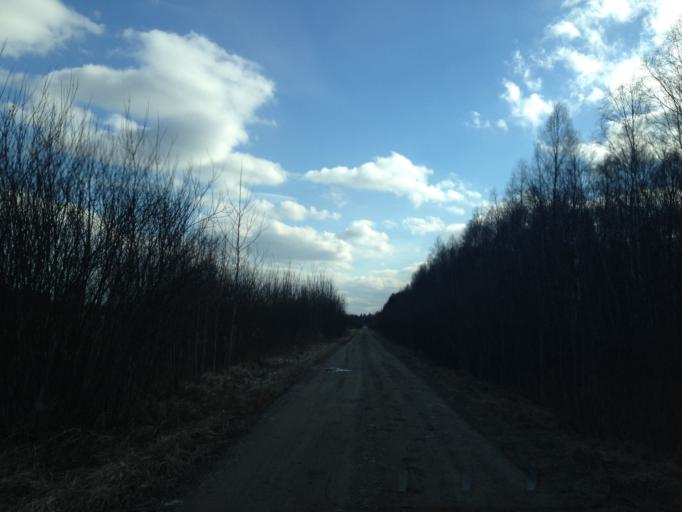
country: EE
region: Harju
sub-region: Keila linn
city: Keila
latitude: 59.1626
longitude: 24.4733
